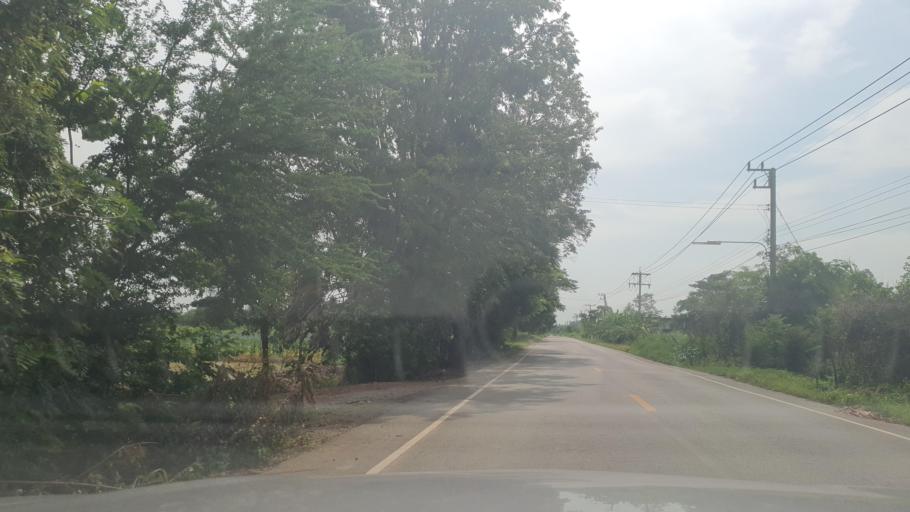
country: TH
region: Sukhothai
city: Si Samrong
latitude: 17.1192
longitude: 99.8653
